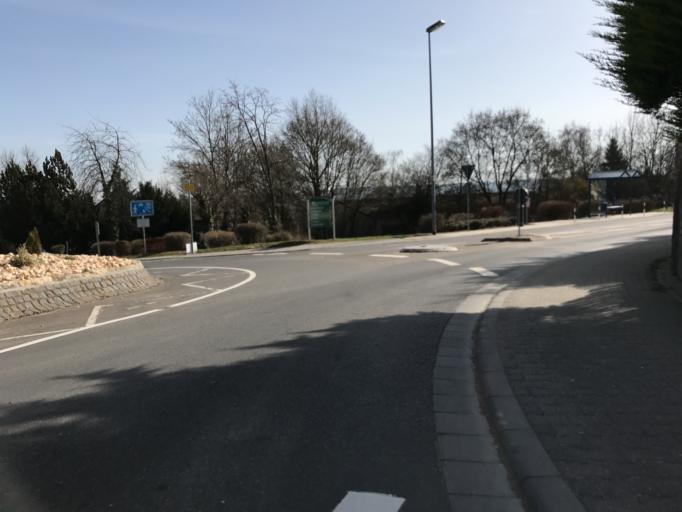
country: DE
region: Rheinland-Pfalz
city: Essenheim
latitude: 49.9267
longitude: 8.1583
